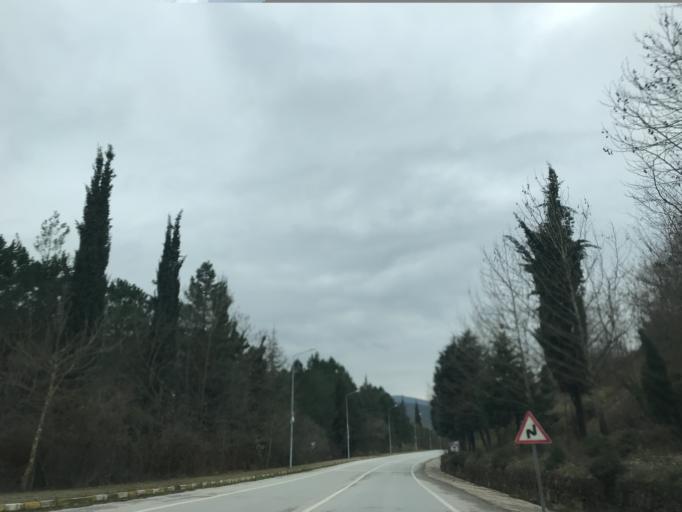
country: TR
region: Yalova
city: Termal
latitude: 40.6040
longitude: 29.1903
